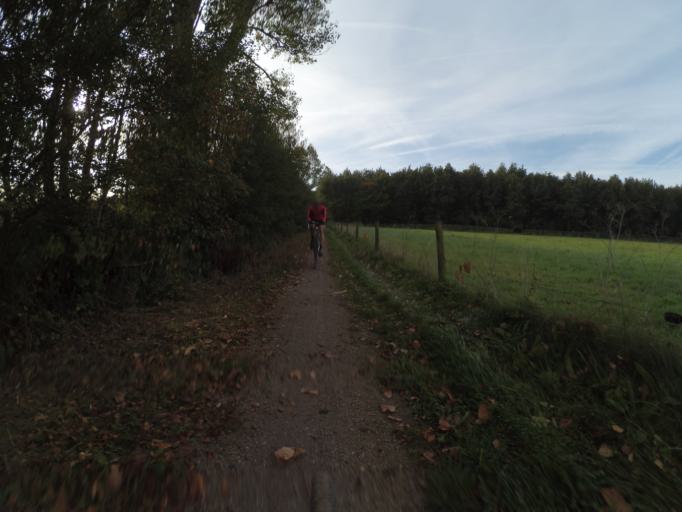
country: NL
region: Gelderland
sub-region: Gemeente Lochem
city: Harfsen
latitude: 52.2750
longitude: 6.3130
